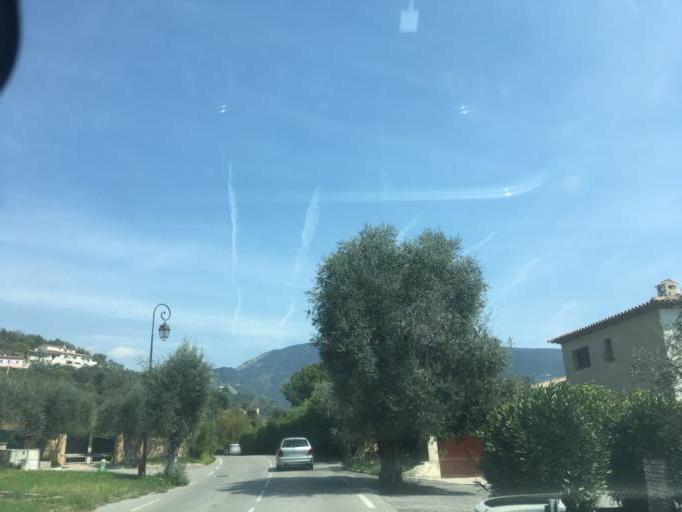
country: FR
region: Provence-Alpes-Cote d'Azur
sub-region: Departement des Alpes-Maritimes
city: Levens
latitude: 43.8446
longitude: 7.2167
